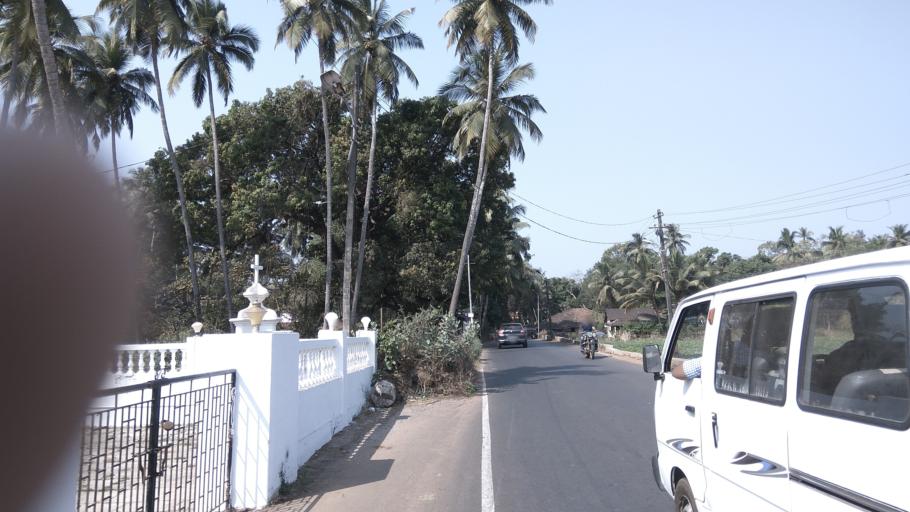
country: IN
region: Goa
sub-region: North Goa
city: Vagator
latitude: 15.5943
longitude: 73.7556
